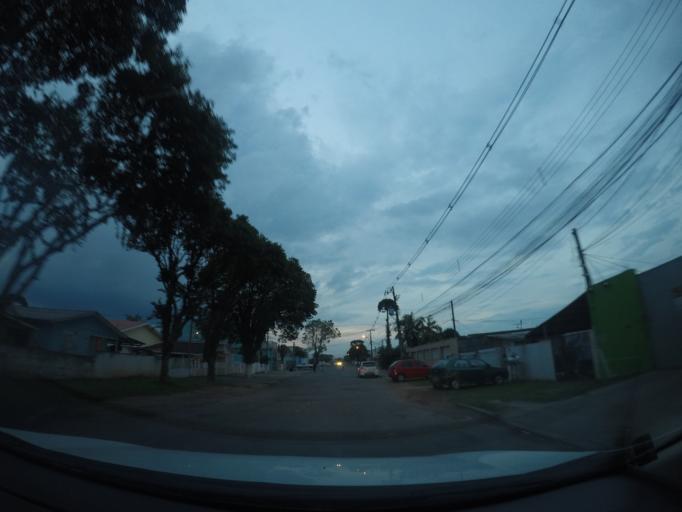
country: BR
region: Parana
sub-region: Sao Jose Dos Pinhais
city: Sao Jose dos Pinhais
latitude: -25.4965
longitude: -49.2317
